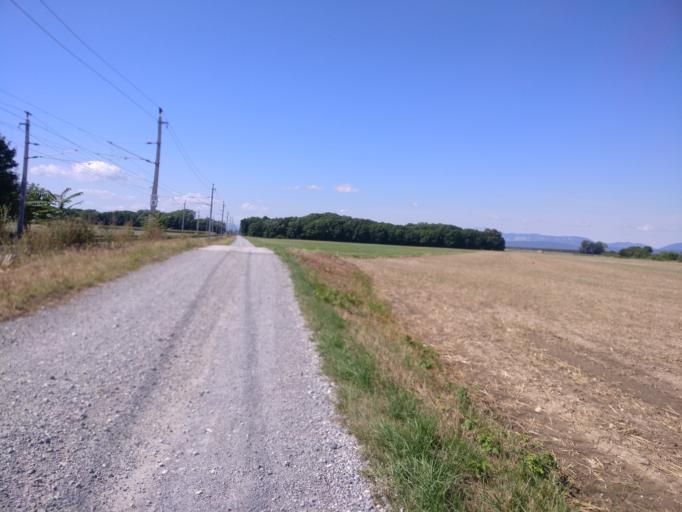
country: AT
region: Lower Austria
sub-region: Politischer Bezirk Wiener Neustadt
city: Zillingdorf
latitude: 47.8723
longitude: 16.3405
